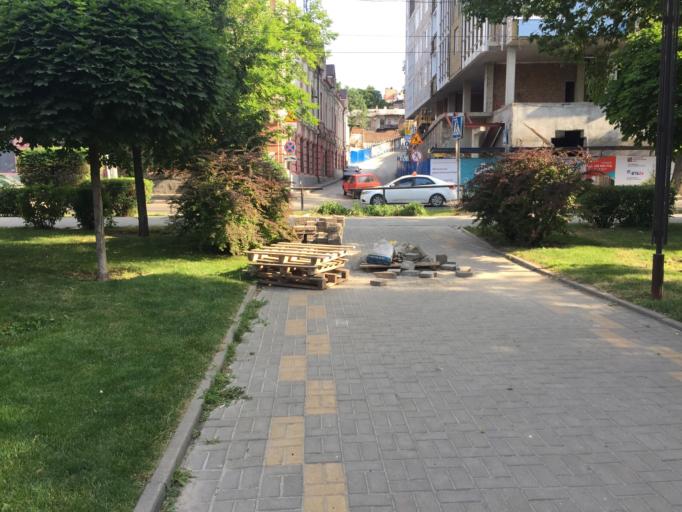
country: RU
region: Rostov
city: Rostov-na-Donu
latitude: 47.2128
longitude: 39.7070
